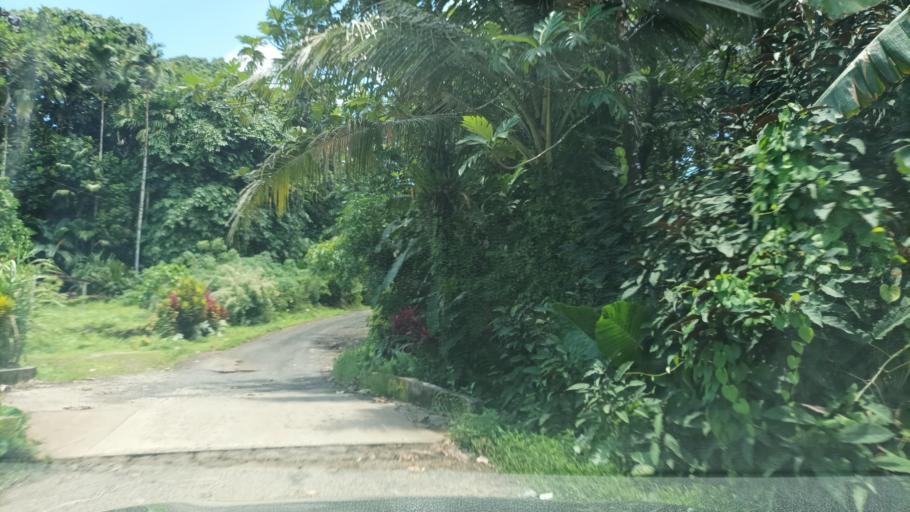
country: FM
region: Pohnpei
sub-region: Madolenihm Municipality
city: Madolenihm Municipality Government
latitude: 6.8459
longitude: 158.3034
